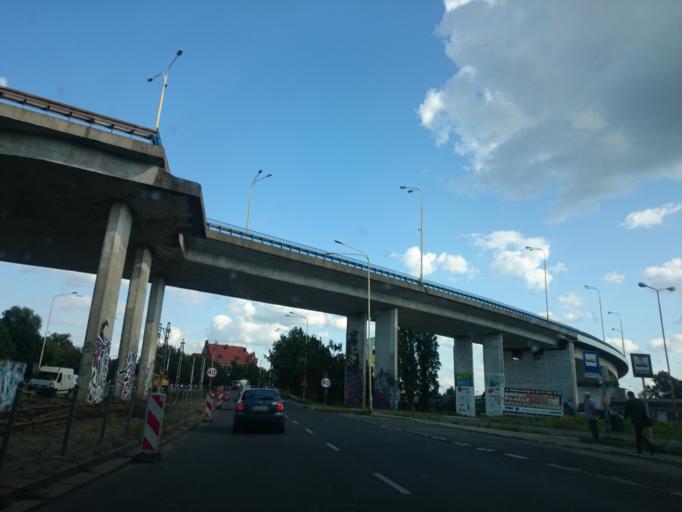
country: PL
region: West Pomeranian Voivodeship
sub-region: Szczecin
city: Szczecin
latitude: 53.4190
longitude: 14.5658
